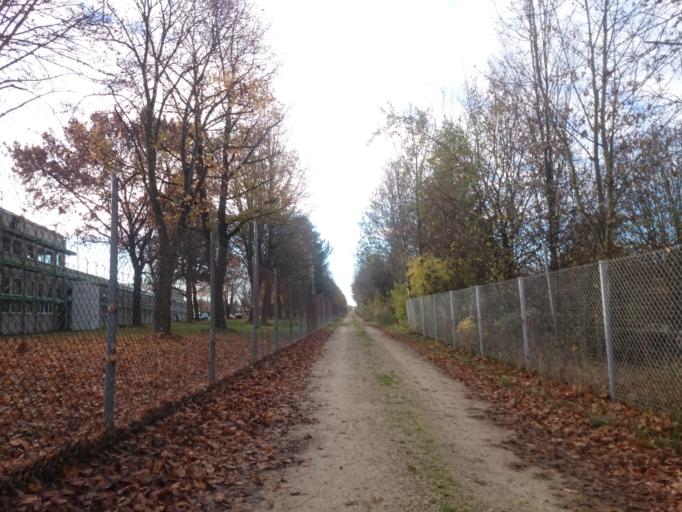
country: DE
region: Bavaria
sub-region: Swabia
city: Konigsbrunn
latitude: 48.2929
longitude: 10.8832
